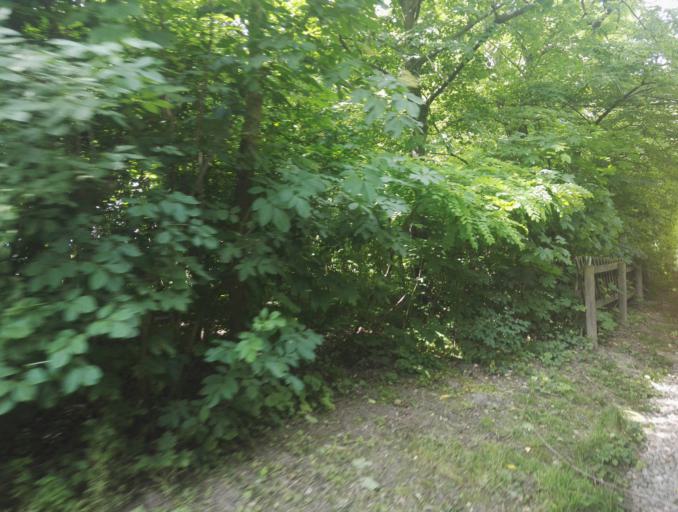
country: AT
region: Vienna
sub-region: Wien Stadt
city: Vienna
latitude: 48.2399
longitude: 16.4106
